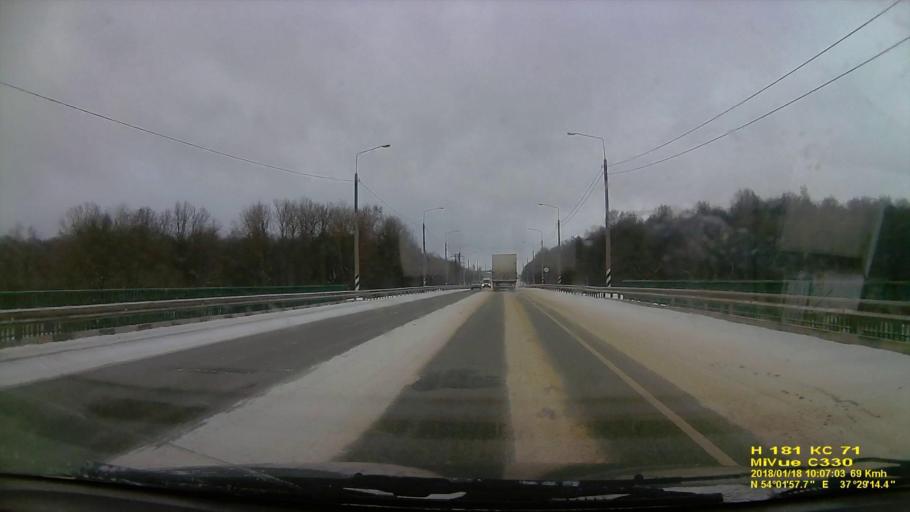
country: RU
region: Tula
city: Pervomayskiy
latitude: 54.0326
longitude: 37.4873
